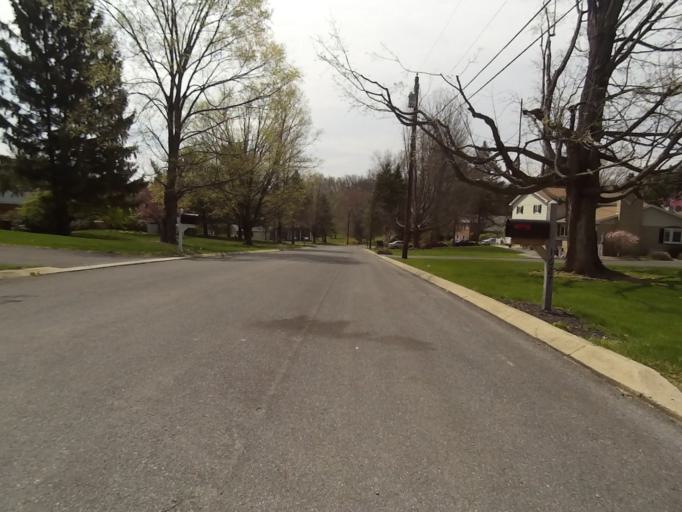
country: US
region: Pennsylvania
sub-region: Centre County
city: Park Forest Village
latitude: 40.7983
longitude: -77.8989
